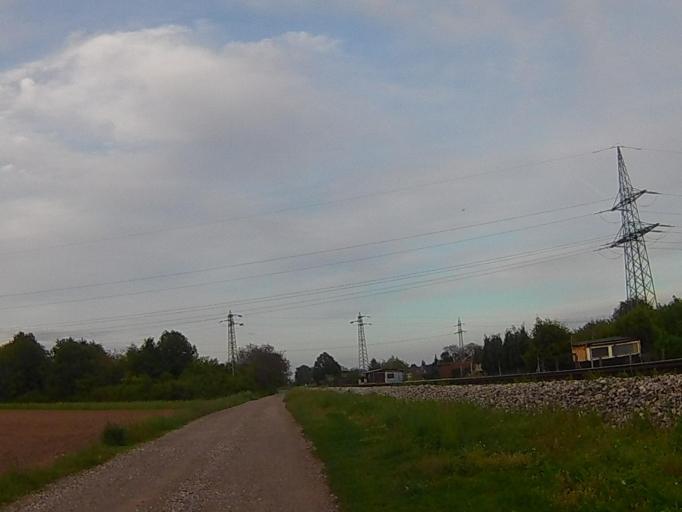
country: SI
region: Maribor
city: Pekre
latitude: 46.5589
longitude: 15.5989
